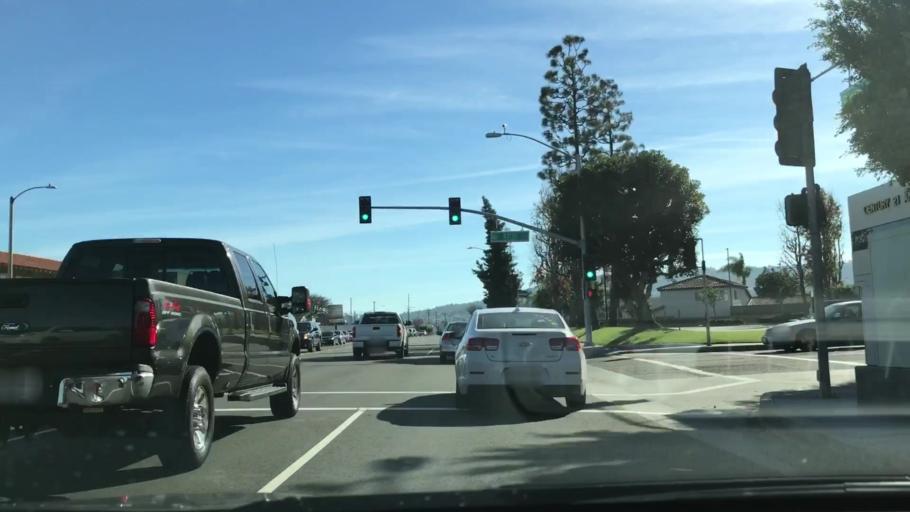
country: US
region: California
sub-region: Los Angeles County
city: Lomita
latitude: 33.8101
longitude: -118.3282
